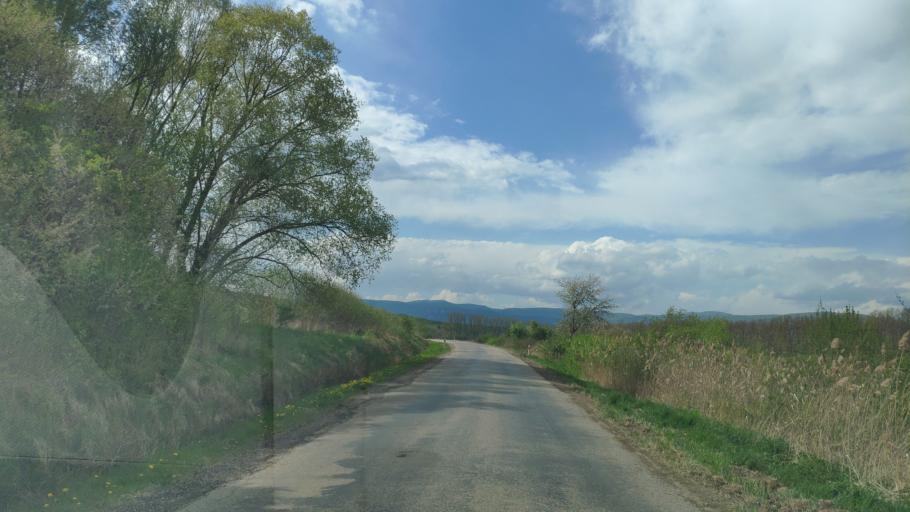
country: SK
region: Kosicky
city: Moldava nad Bodvou
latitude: 48.5624
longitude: 20.9515
